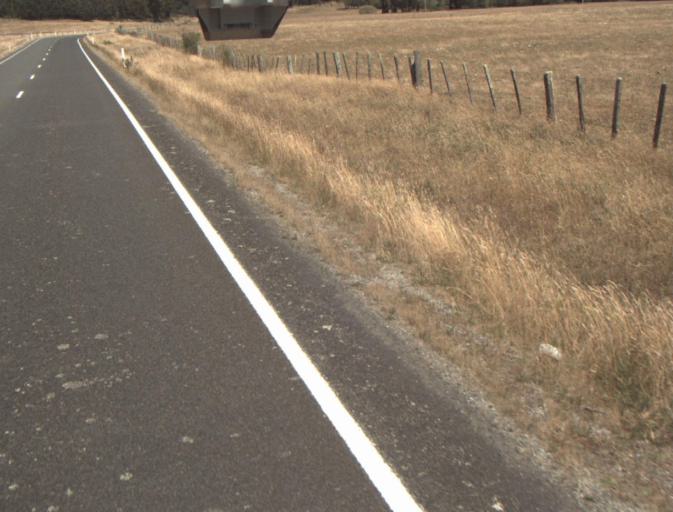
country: AU
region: Tasmania
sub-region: Dorset
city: Scottsdale
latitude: -41.2913
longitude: 147.3851
